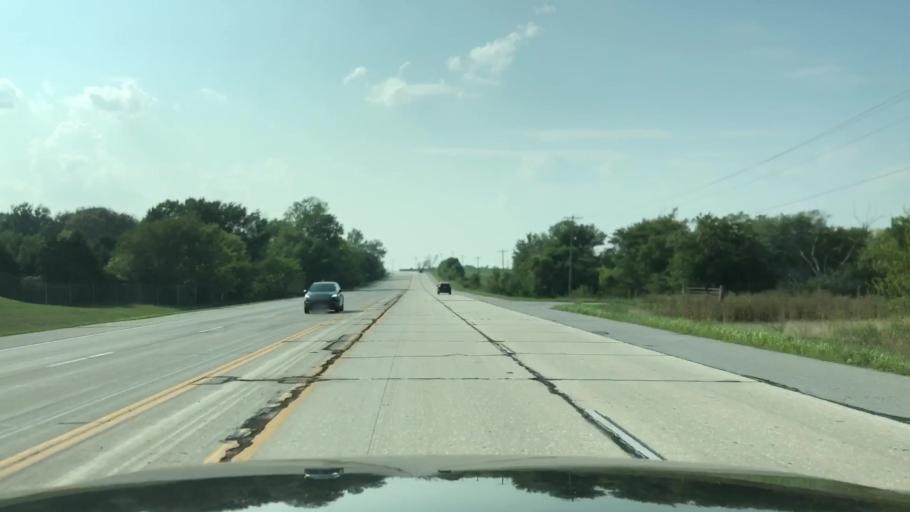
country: US
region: Missouri
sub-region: Saint Charles County
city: Wentzville
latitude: 38.8249
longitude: -90.8247
